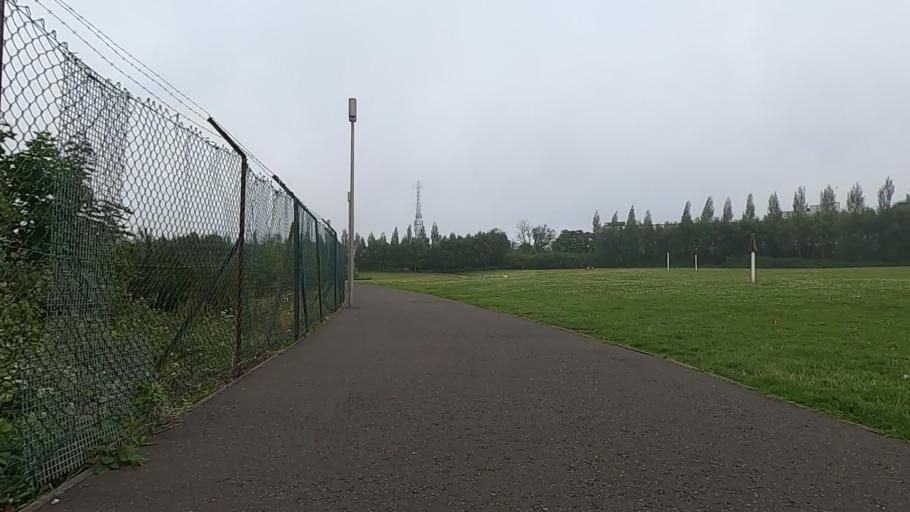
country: GB
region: Scotland
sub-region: Edinburgh
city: Edinburgh
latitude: 55.9790
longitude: -3.2505
